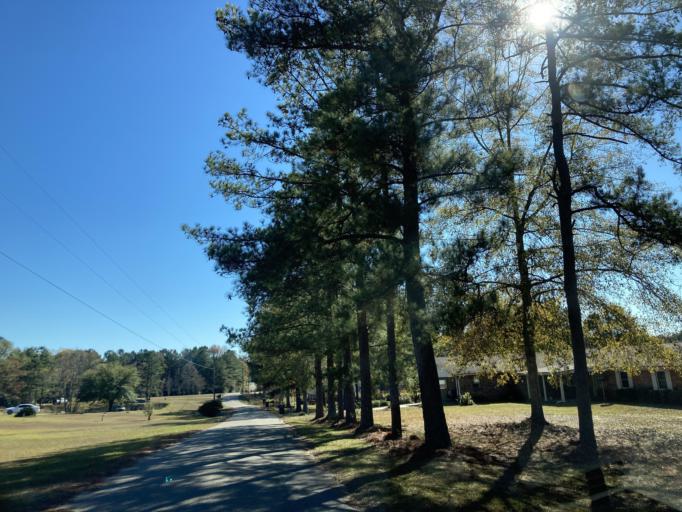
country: US
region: Mississippi
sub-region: Lamar County
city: Sumrall
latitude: 31.2915
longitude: -89.6457
